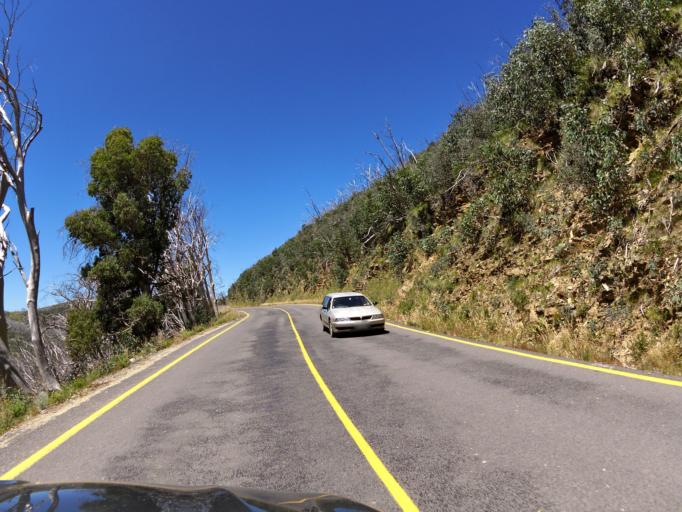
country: AU
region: Victoria
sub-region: Alpine
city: Mount Beauty
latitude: -37.0031
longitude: 147.0739
